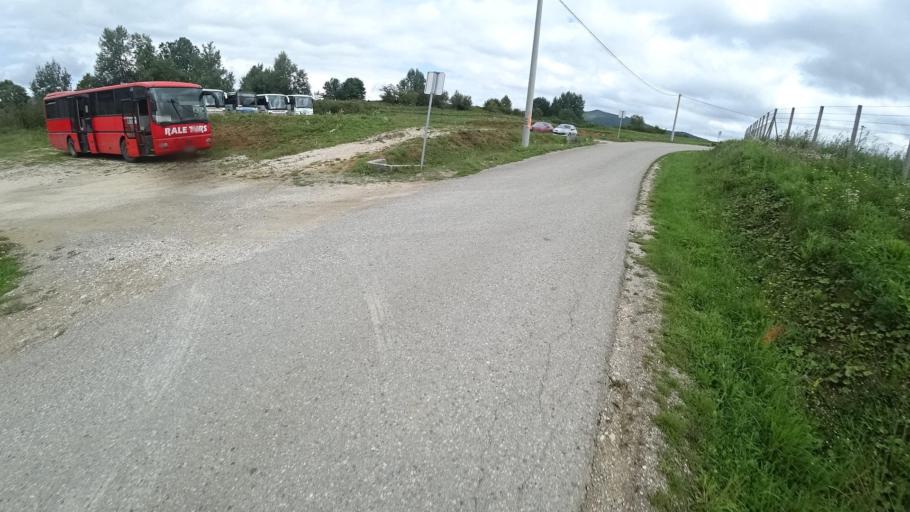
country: BA
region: Republika Srpska
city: Bronzani Majdan
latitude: 44.6648
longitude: 17.0034
